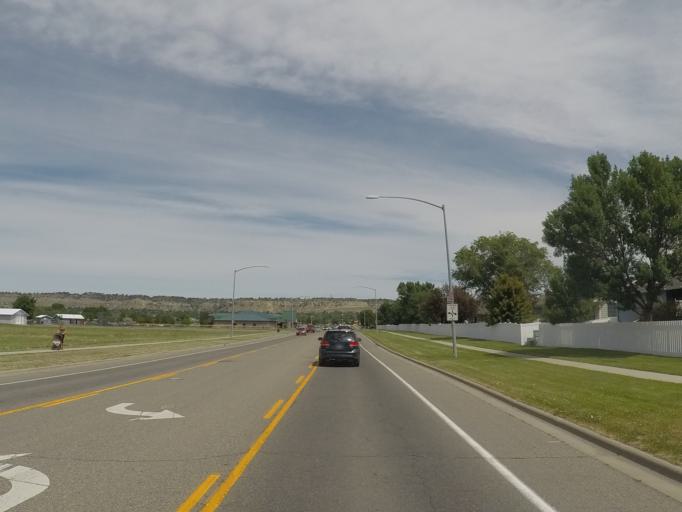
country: US
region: Montana
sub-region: Yellowstone County
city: Billings
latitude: 45.7724
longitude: -108.5969
